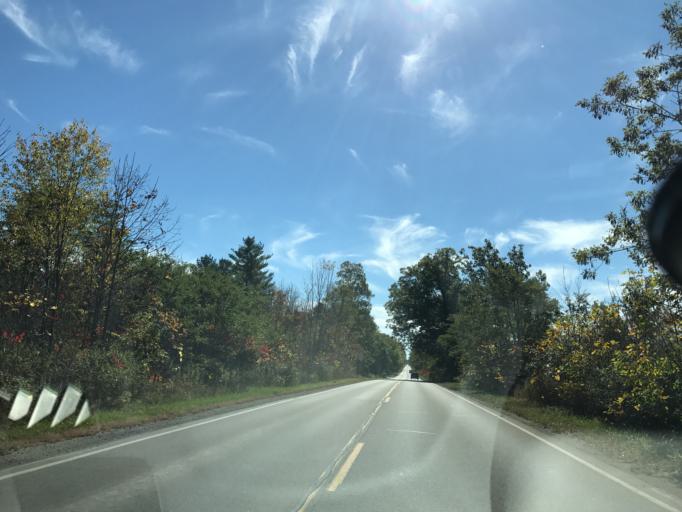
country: US
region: Michigan
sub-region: Oakland County
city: South Lyon
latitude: 42.4126
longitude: -83.6464
